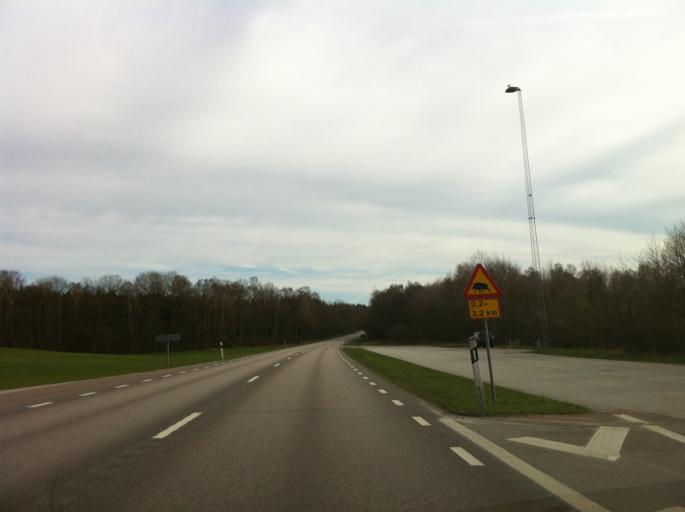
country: SE
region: Skane
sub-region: Bjuvs Kommun
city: Billesholm
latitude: 56.0424
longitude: 12.9692
